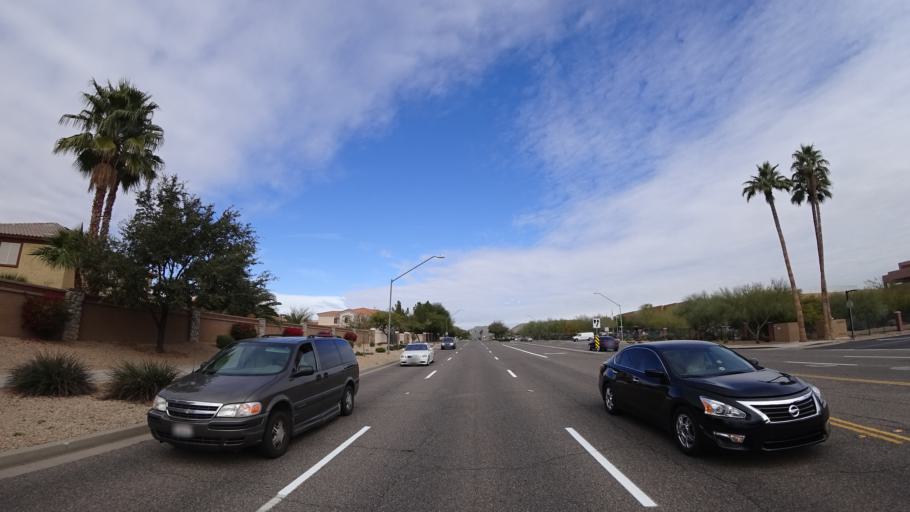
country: US
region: Arizona
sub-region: Maricopa County
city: Peoria
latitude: 33.6591
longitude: -112.1865
